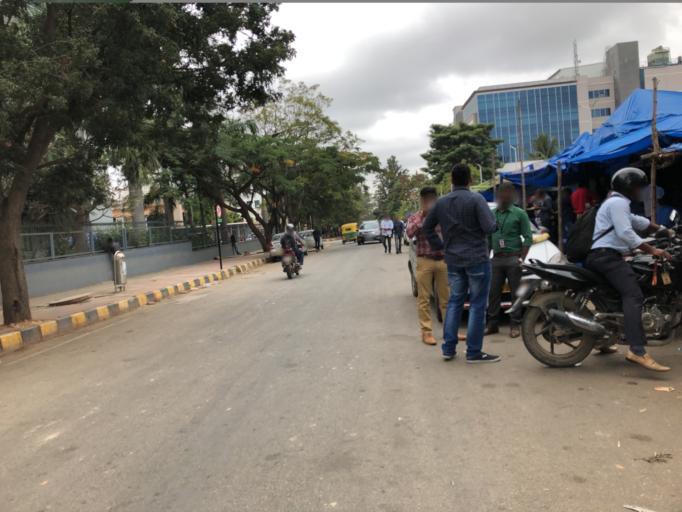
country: IN
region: Karnataka
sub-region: Bangalore Rural
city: Hoskote
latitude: 12.9845
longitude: 77.7286
